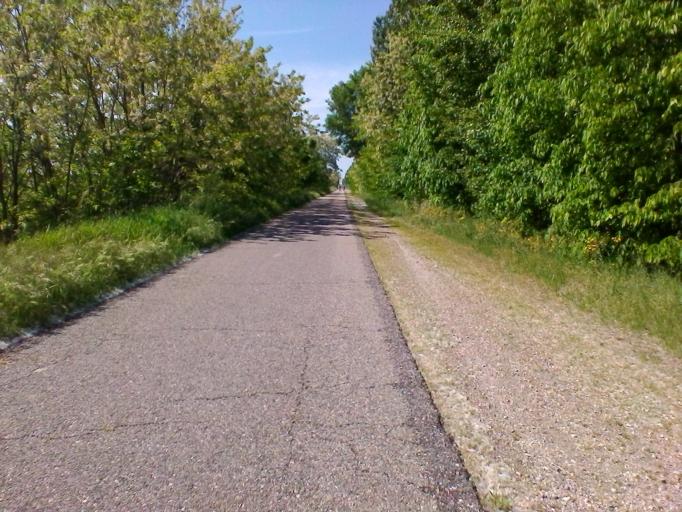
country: IT
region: Lombardy
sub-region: Provincia di Mantova
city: Soave
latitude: 45.2180
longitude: 10.7180
